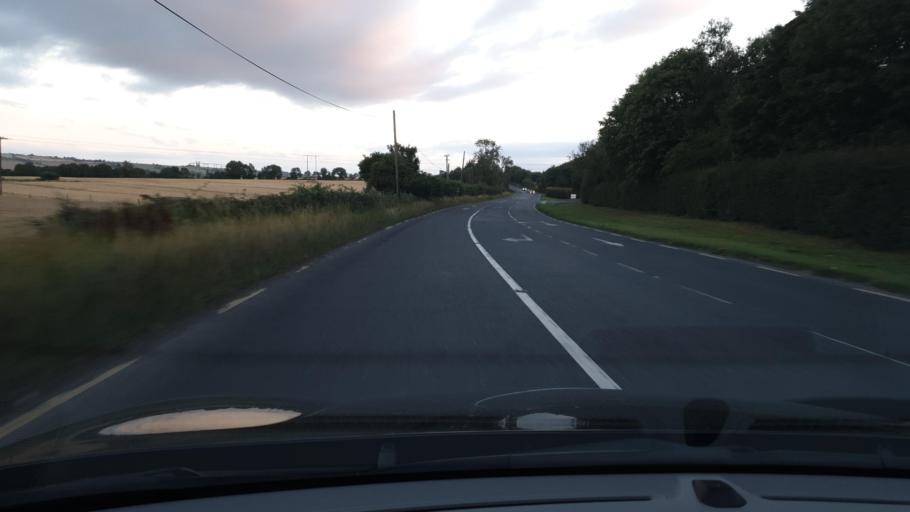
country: IE
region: Leinster
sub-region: An Mhi
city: Duleek
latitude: 53.6823
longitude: -6.3833
